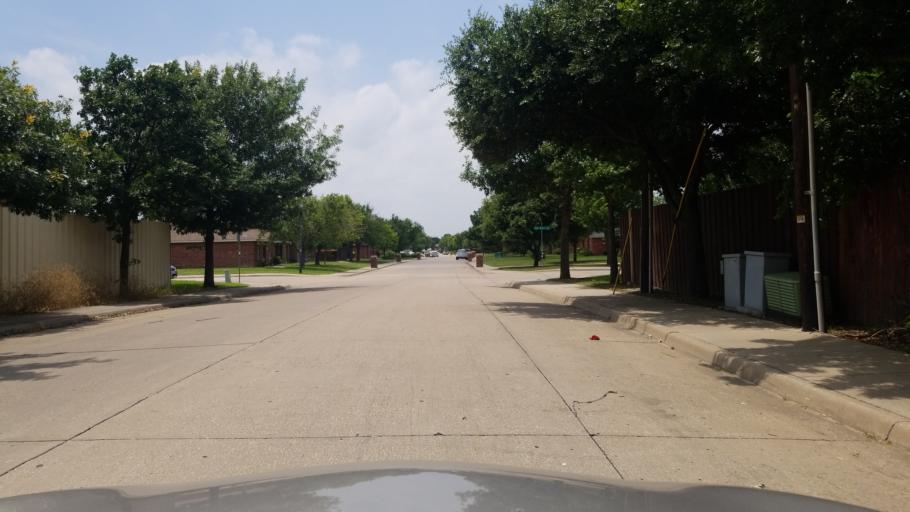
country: US
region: Texas
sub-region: Dallas County
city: Duncanville
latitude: 32.6855
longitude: -96.9127
